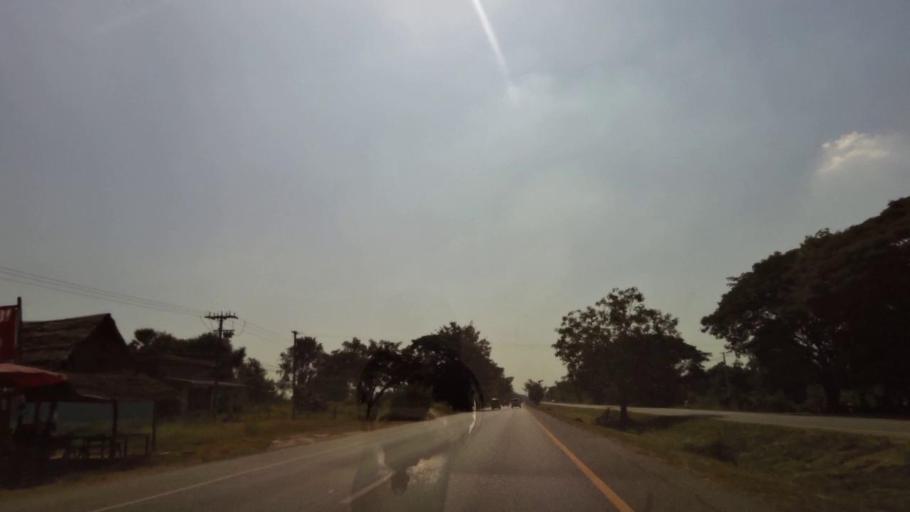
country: TH
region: Phichit
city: Wachira Barami
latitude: 16.3873
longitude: 100.1378
